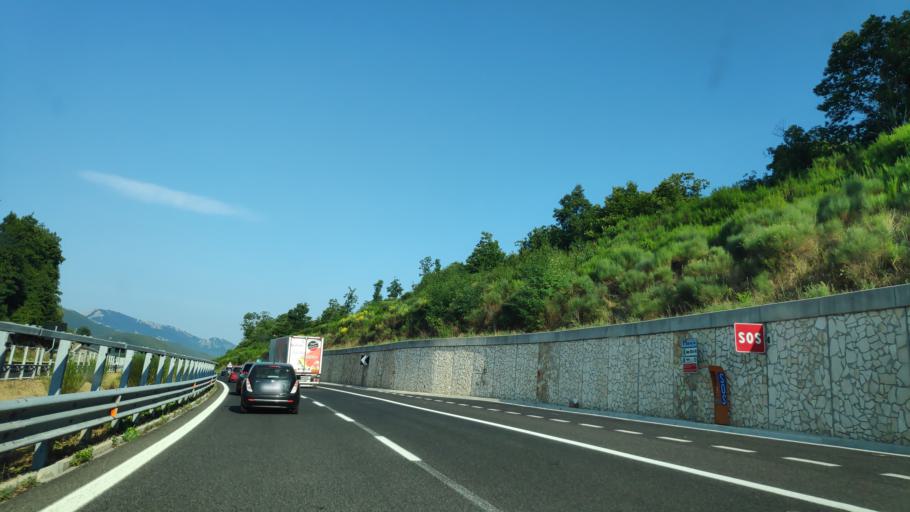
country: IT
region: Basilicate
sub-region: Provincia di Potenza
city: Lagonegro
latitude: 40.1289
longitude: 15.7731
